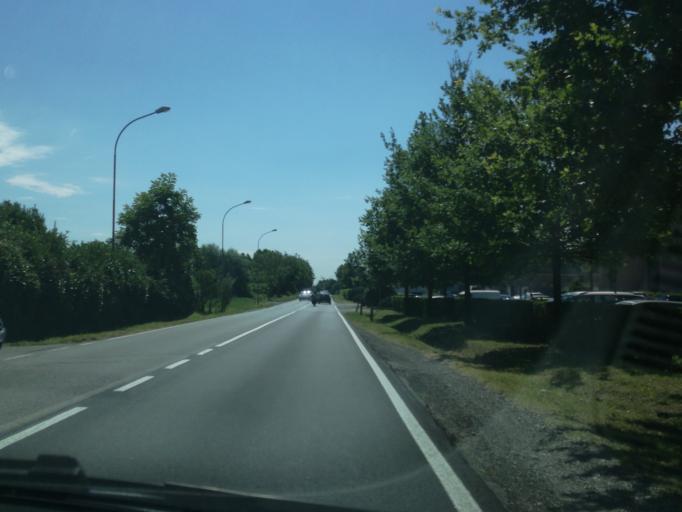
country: IT
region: Lombardy
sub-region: Provincia di Bergamo
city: Piazza Caduti
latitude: 45.6980
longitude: 9.4993
